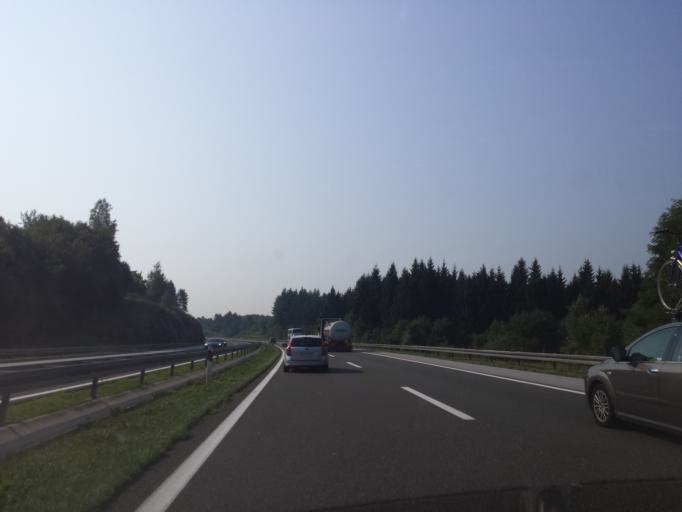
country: HR
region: Karlovacka
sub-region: Grad Ogulin
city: Ogulin
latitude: 45.3864
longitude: 15.2599
